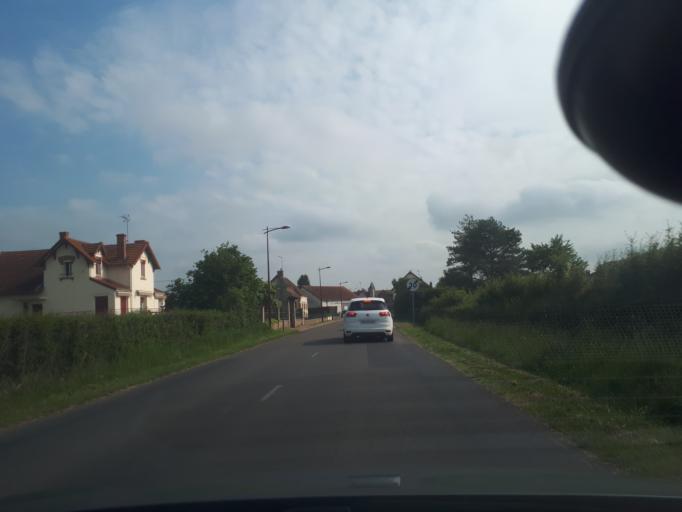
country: FR
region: Auvergne
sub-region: Departement de l'Allier
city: Dompierre-sur-Besbre
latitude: 46.4434
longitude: 3.6287
